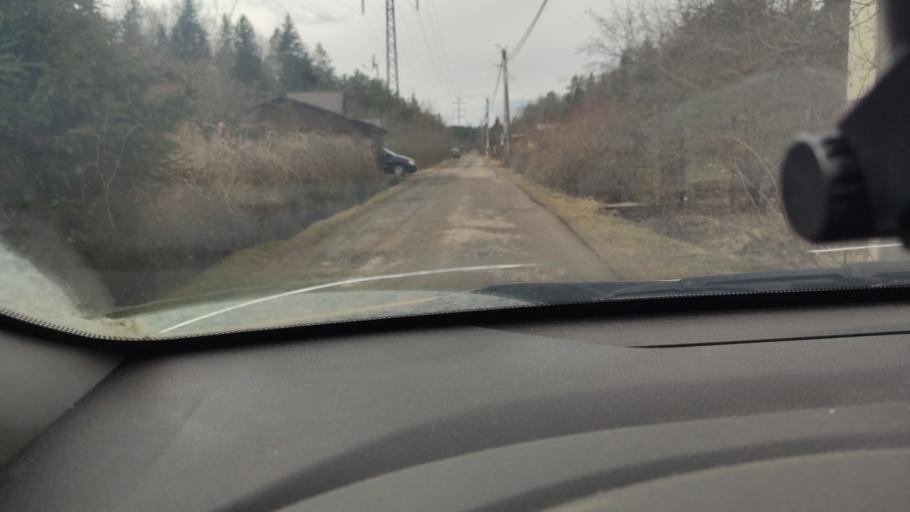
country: RU
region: Moskovskaya
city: Chupryakovo
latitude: 55.5830
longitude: 36.6014
